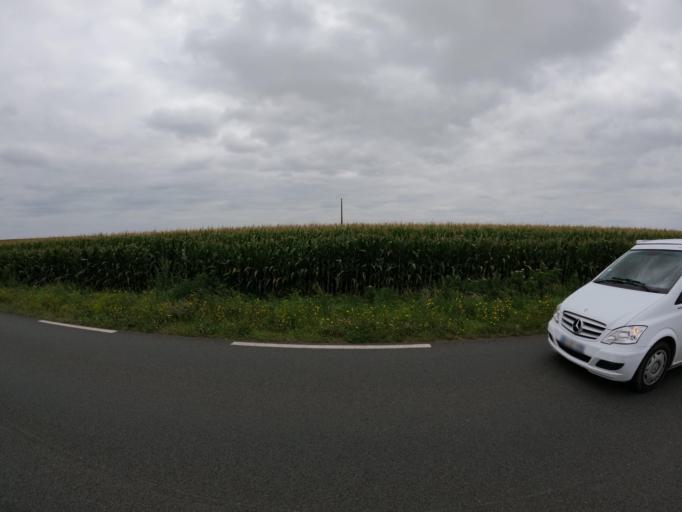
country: FR
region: Pays de la Loire
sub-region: Departement de la Vendee
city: Sainte-Hermine
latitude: 46.5399
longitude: -1.0232
